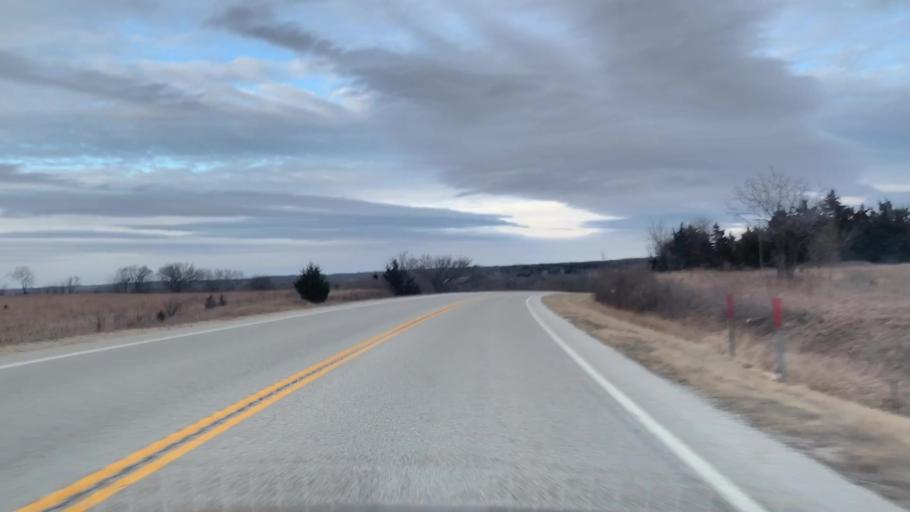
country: US
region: Kansas
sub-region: Anderson County
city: Garnett
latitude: 38.3876
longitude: -95.1096
